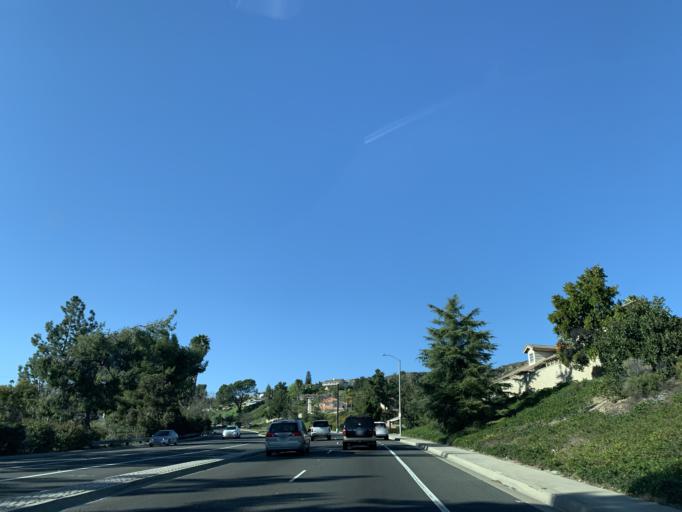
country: US
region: California
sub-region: Los Angeles County
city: Walnut
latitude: 34.0484
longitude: -117.8503
